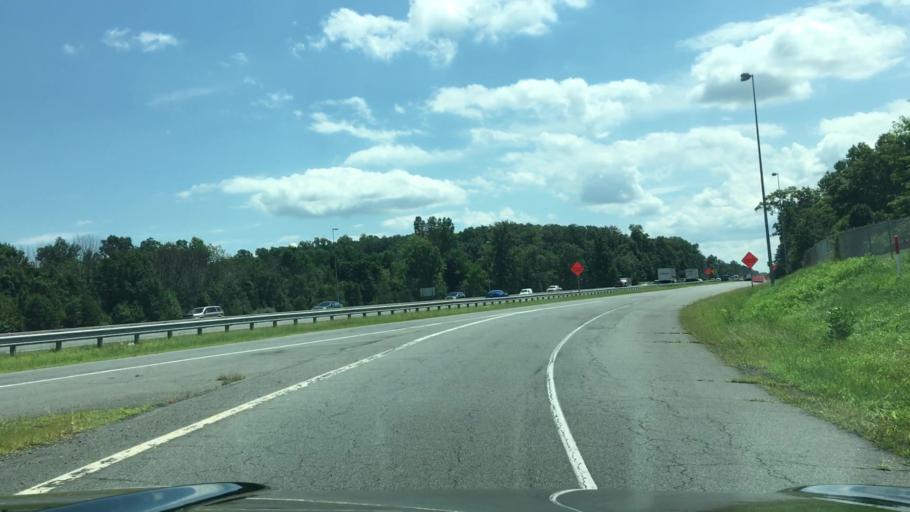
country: US
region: Virginia
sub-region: Fairfax County
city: Chantilly
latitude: 38.8709
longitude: -77.4444
